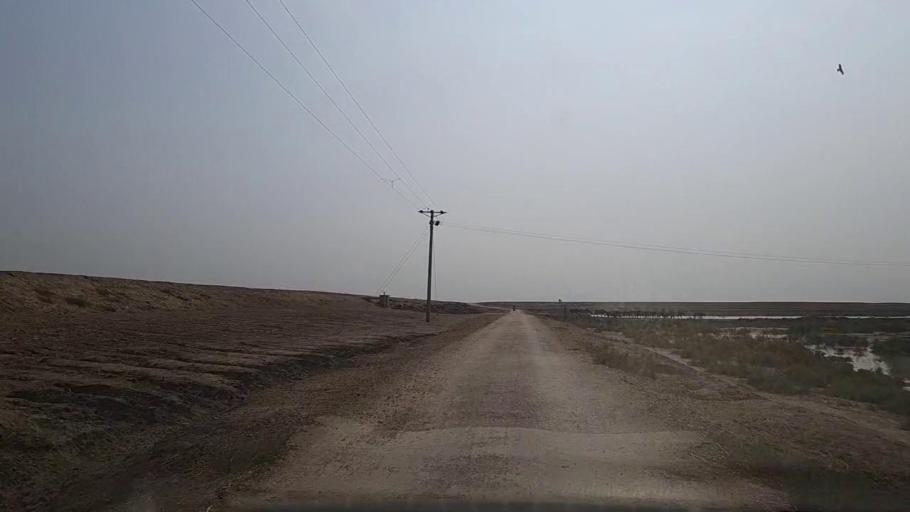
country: PK
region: Sindh
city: Thatta
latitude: 24.5750
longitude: 67.9160
